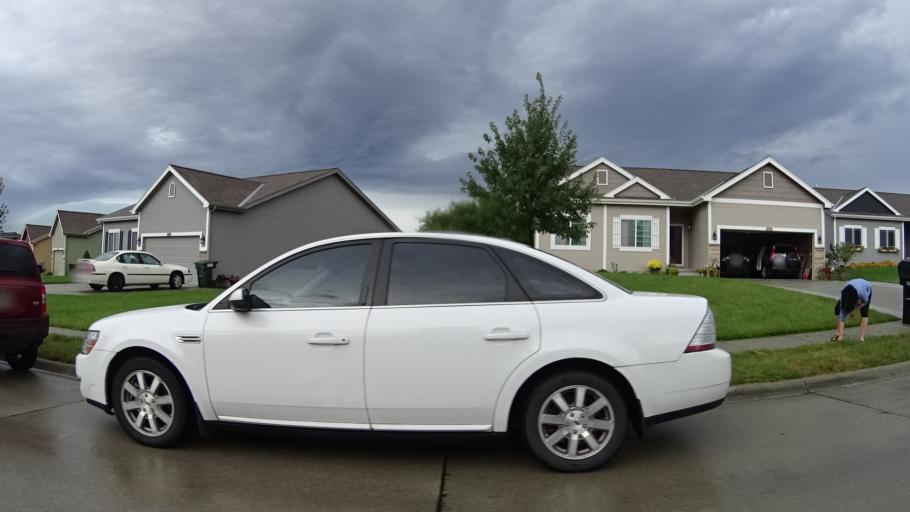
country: US
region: Nebraska
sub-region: Sarpy County
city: Offutt Air Force Base
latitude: 41.1563
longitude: -95.9518
